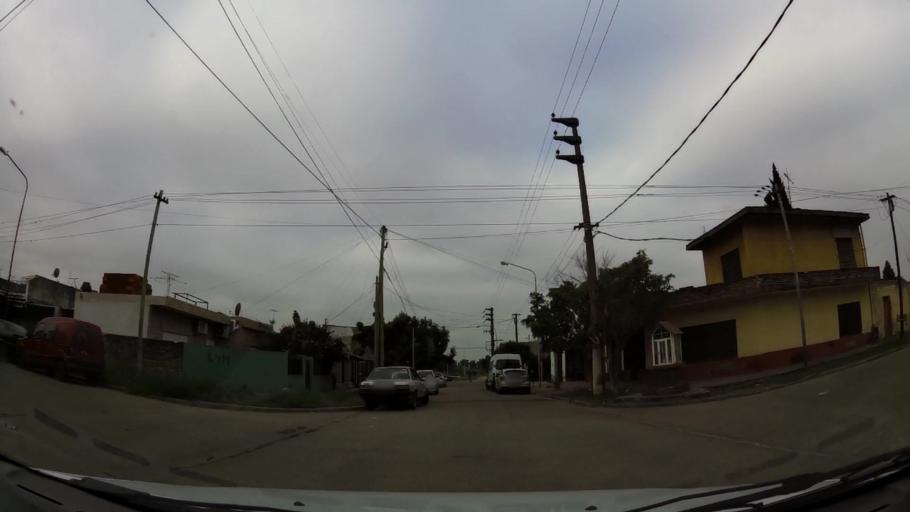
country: AR
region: Buenos Aires
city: San Justo
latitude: -34.7037
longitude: -58.5554
